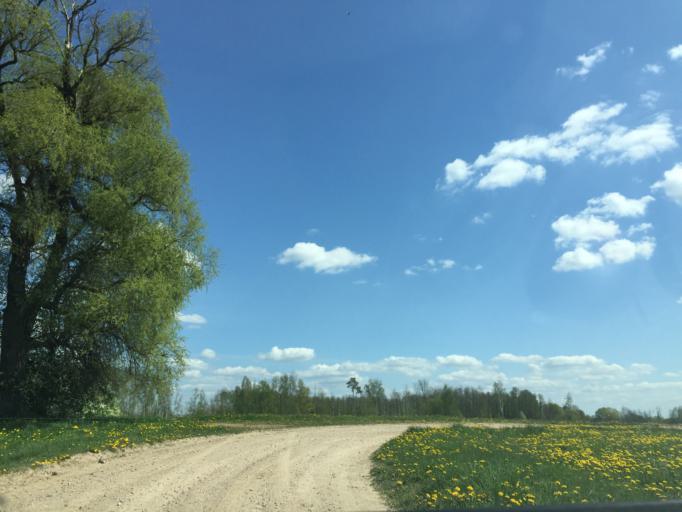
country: LV
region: Vecumnieki
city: Vecumnieki
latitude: 56.4688
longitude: 24.5959
